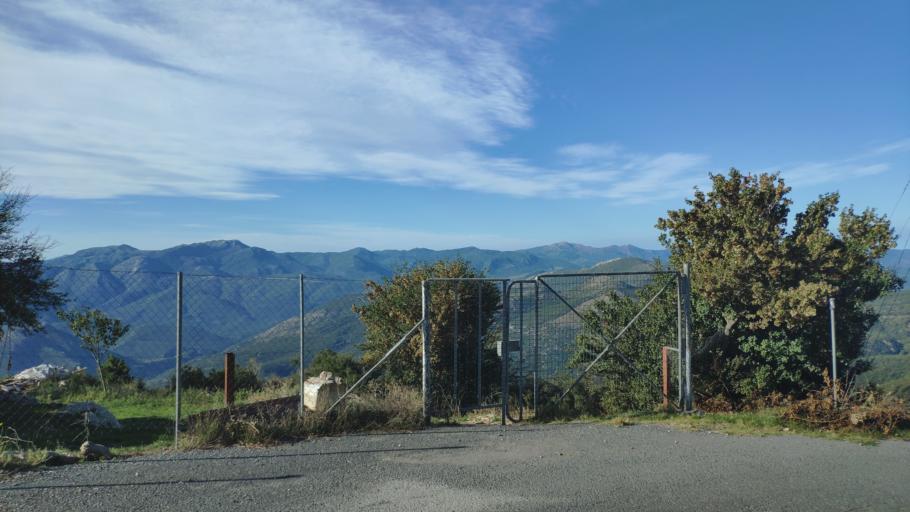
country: GR
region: Peloponnese
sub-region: Nomos Arkadias
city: Dimitsana
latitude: 37.5489
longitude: 22.0655
